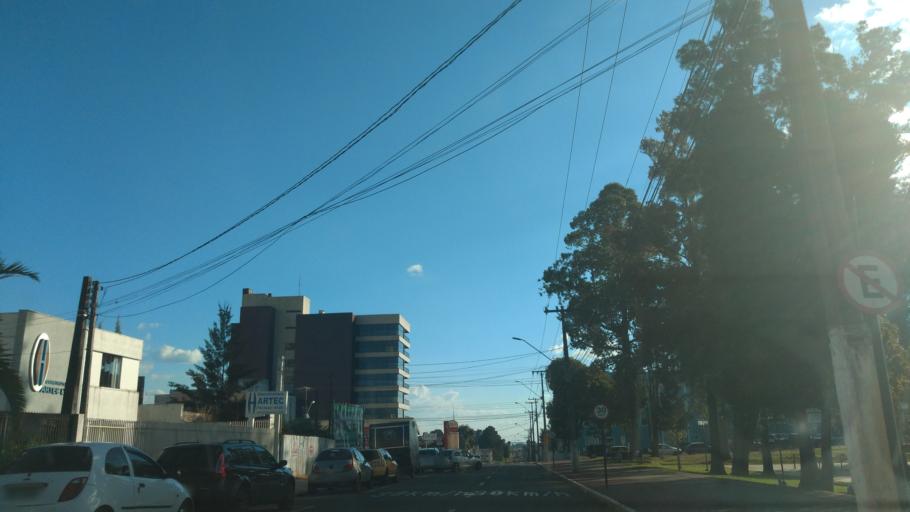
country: BR
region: Parana
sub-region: Guarapuava
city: Guarapuava
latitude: -25.3961
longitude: -51.4619
